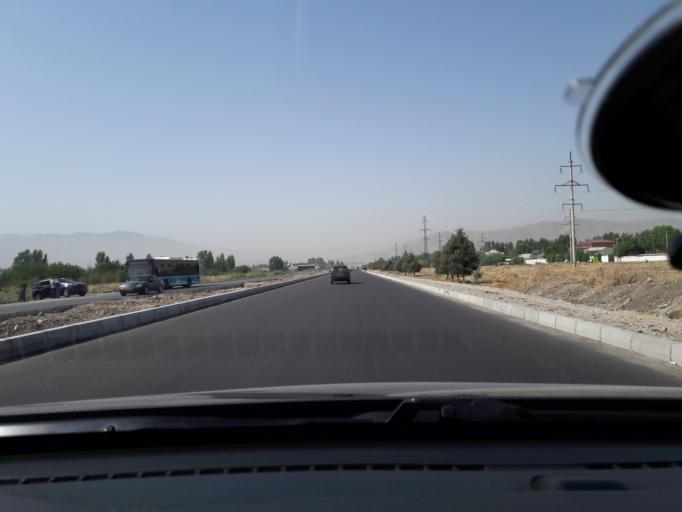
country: TJ
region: Dushanbe
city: Dushanbe
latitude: 38.4884
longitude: 68.7503
